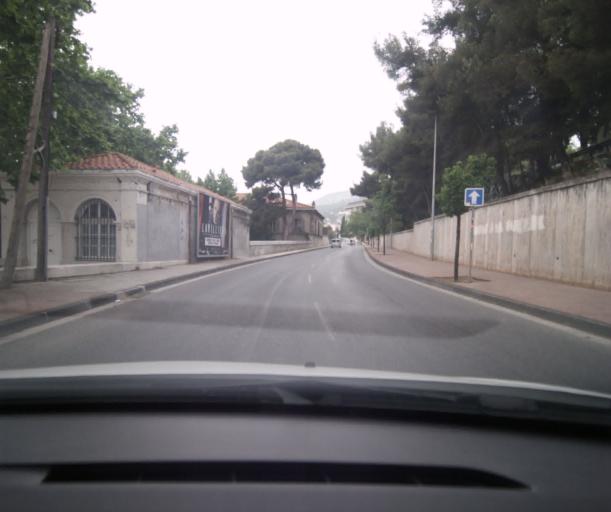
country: FR
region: Provence-Alpes-Cote d'Azur
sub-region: Departement du Var
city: Toulon
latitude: 43.1270
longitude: 5.9352
